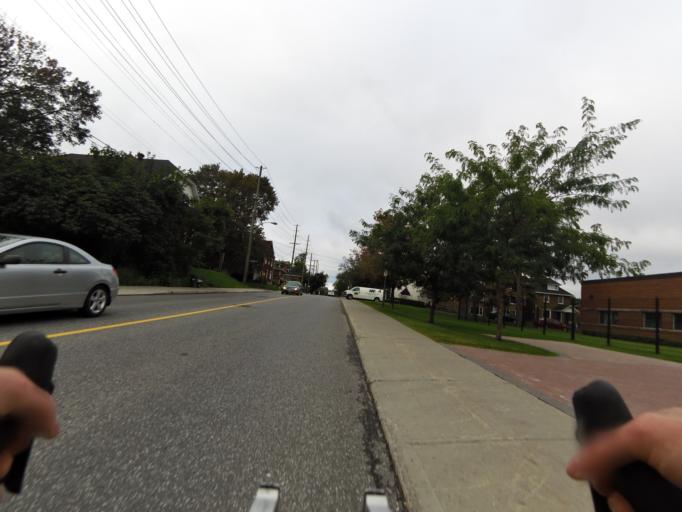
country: CA
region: Ontario
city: Ottawa
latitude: 45.4032
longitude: -75.7164
